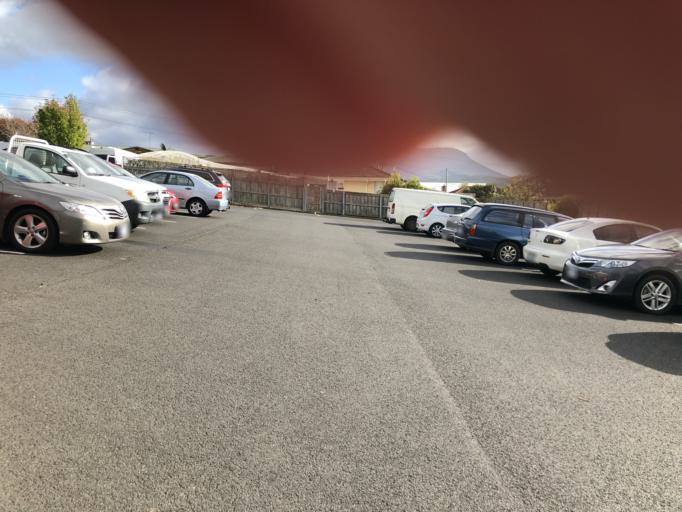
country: AU
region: Tasmania
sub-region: Kingborough
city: Kingston
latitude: -42.9782
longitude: 147.3063
